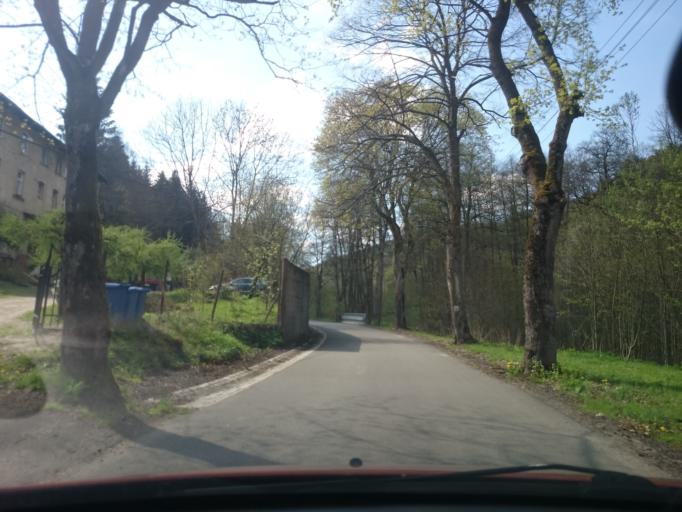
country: PL
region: Lower Silesian Voivodeship
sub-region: Powiat klodzki
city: Polanica-Zdroj
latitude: 50.3023
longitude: 16.5376
